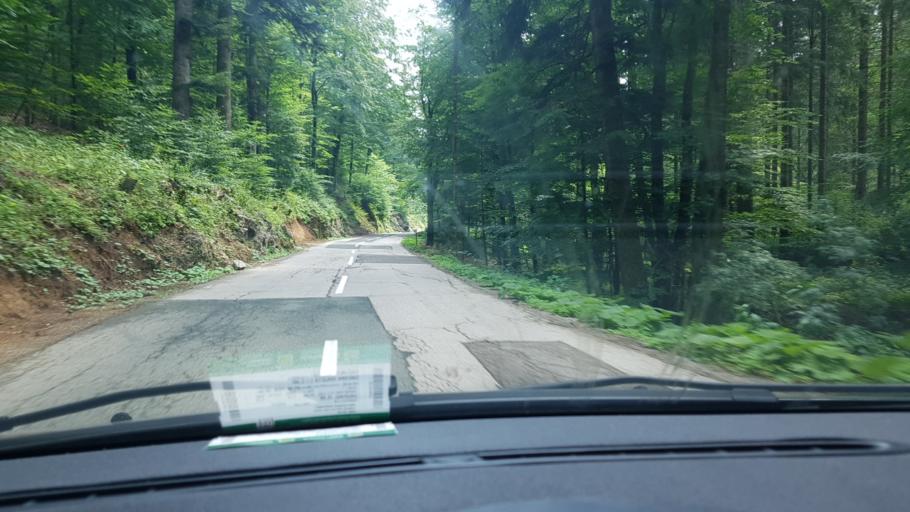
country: HR
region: Primorsko-Goranska
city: Hreljin
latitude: 45.3380
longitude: 14.6756
